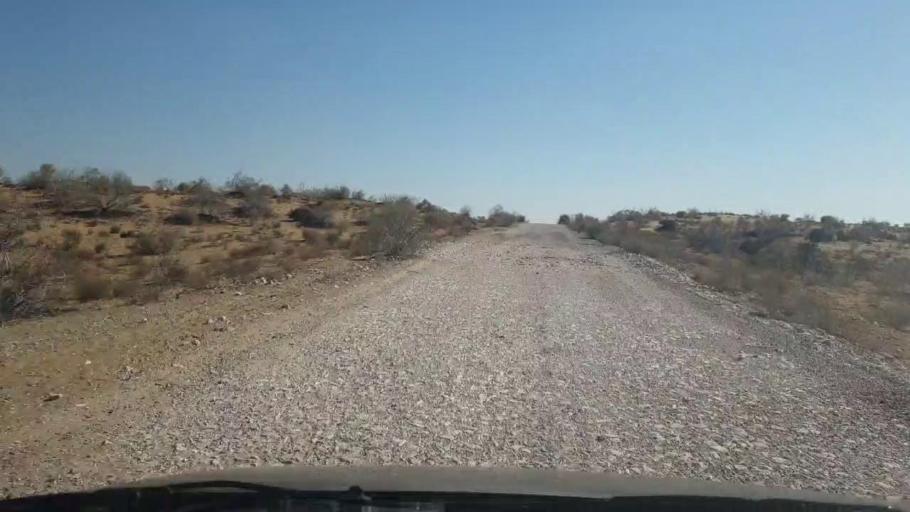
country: PK
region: Sindh
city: Bozdar
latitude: 27.0268
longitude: 68.7099
